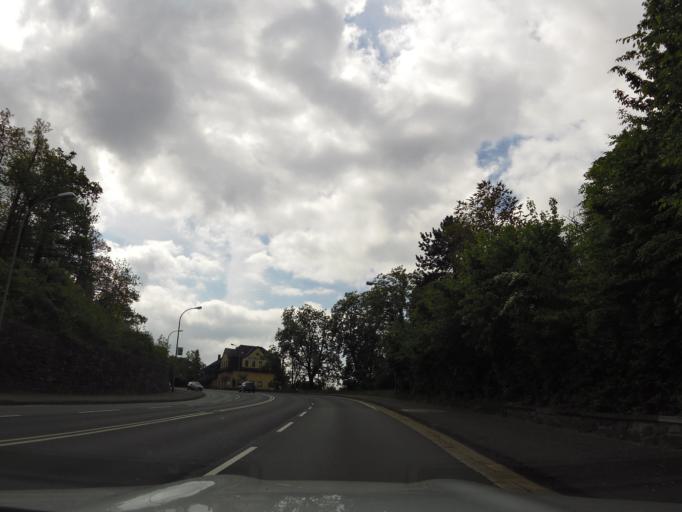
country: DE
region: Hesse
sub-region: Regierungsbezirk Giessen
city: Wetzlar
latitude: 50.5509
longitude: 8.5170
